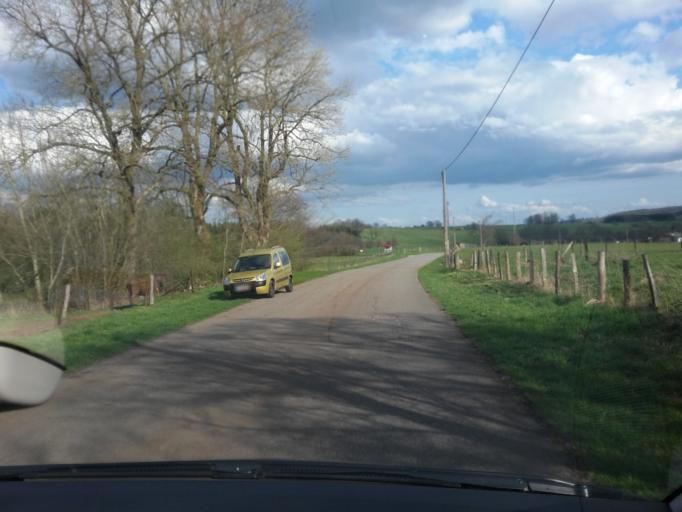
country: BE
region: Wallonia
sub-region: Province du Luxembourg
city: Florenville
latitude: 49.7219
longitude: 5.2551
